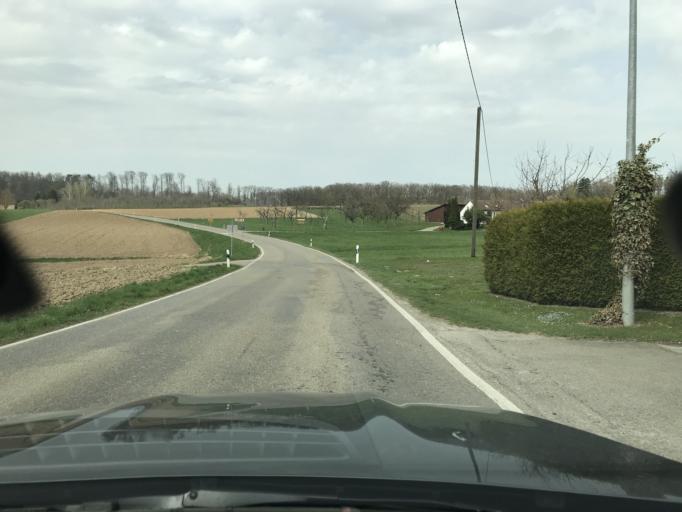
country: DE
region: Baden-Wuerttemberg
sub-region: Regierungsbezirk Stuttgart
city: Burgstetten
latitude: 48.9131
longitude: 9.3809
